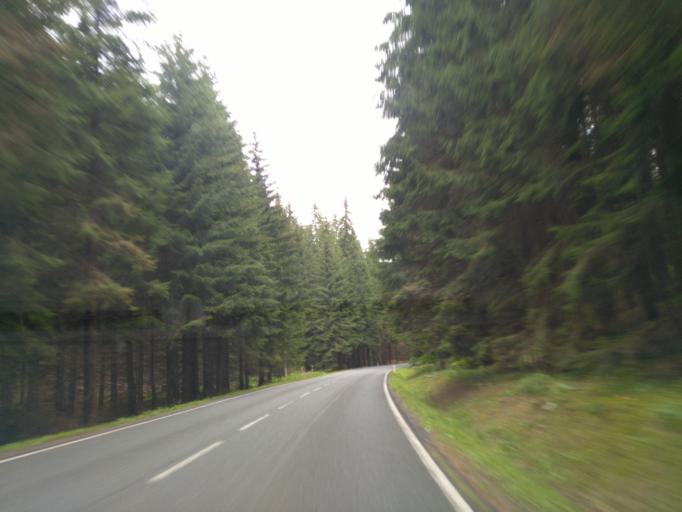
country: DE
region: Saxony
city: Johanngeorgenstadt
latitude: 50.4098
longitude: 12.7359
